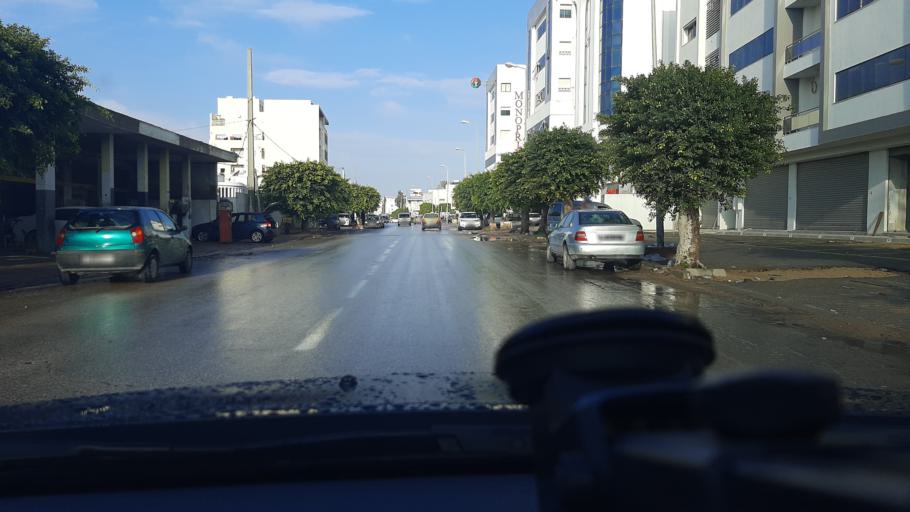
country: TN
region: Safaqis
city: Sfax
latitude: 34.7446
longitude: 10.7452
